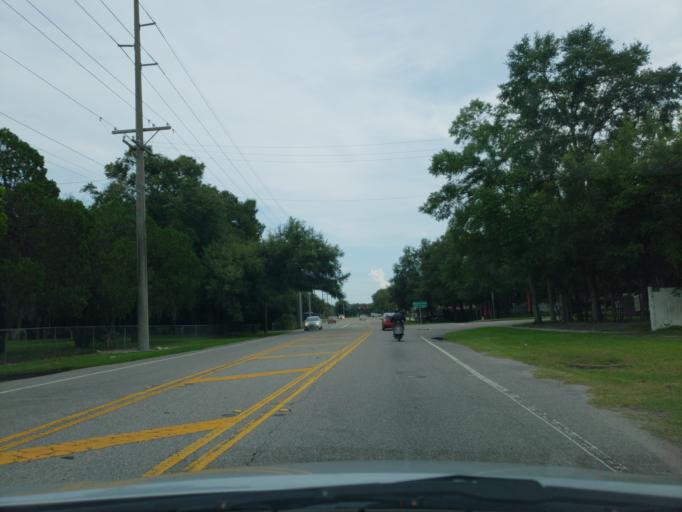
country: US
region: Florida
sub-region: Hillsborough County
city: University
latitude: 28.0832
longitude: -82.4308
